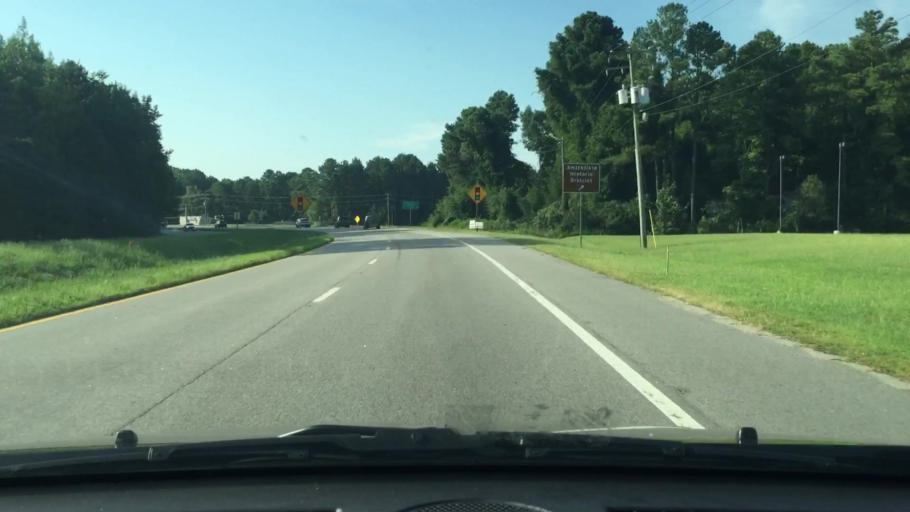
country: US
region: Virginia
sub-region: Isle of Wight County
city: Carrollton
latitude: 36.9433
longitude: -76.5378
